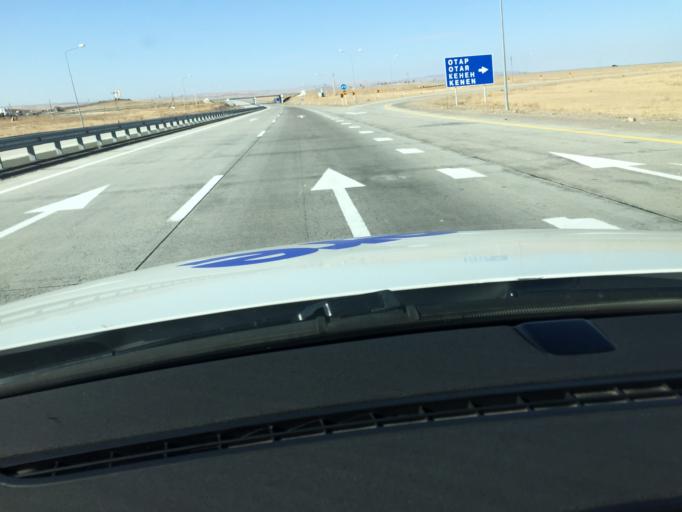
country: KG
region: Chuy
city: Ivanovka
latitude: 43.4076
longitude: 75.0942
